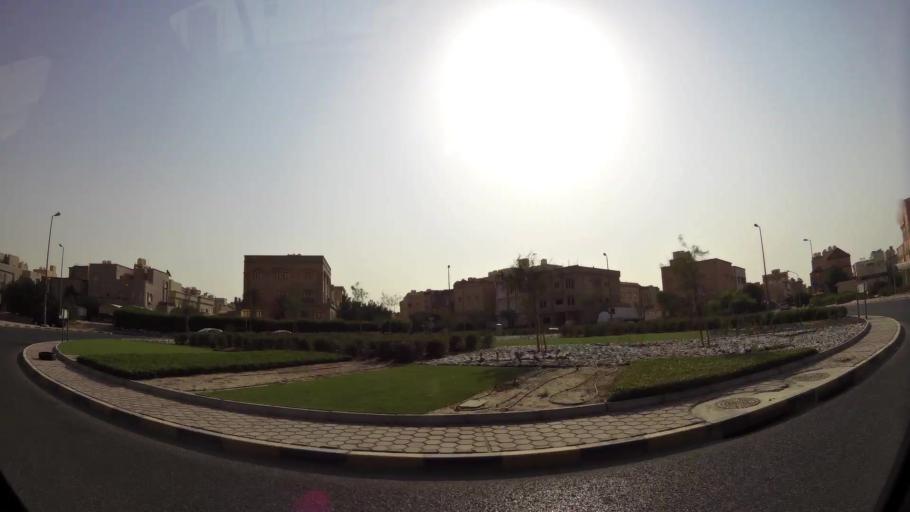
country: KW
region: Al Asimah
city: Ar Rabiyah
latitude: 29.3074
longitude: 47.7961
